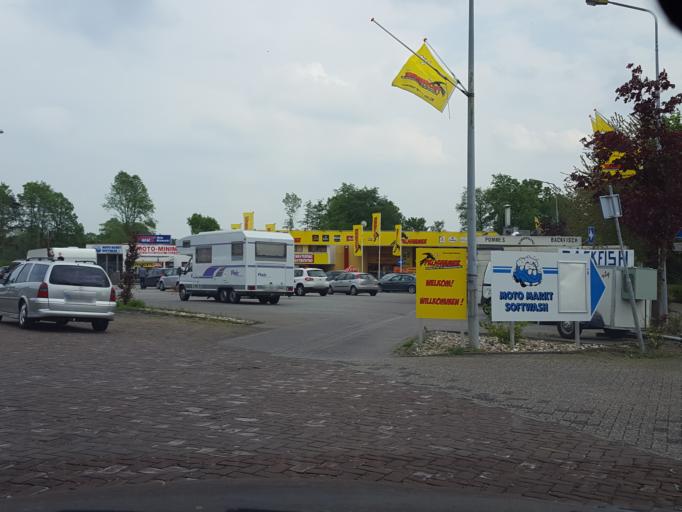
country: NL
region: Gelderland
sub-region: Gemeente Winterswijk
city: Winterswijk
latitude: 51.9608
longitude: 6.7328
